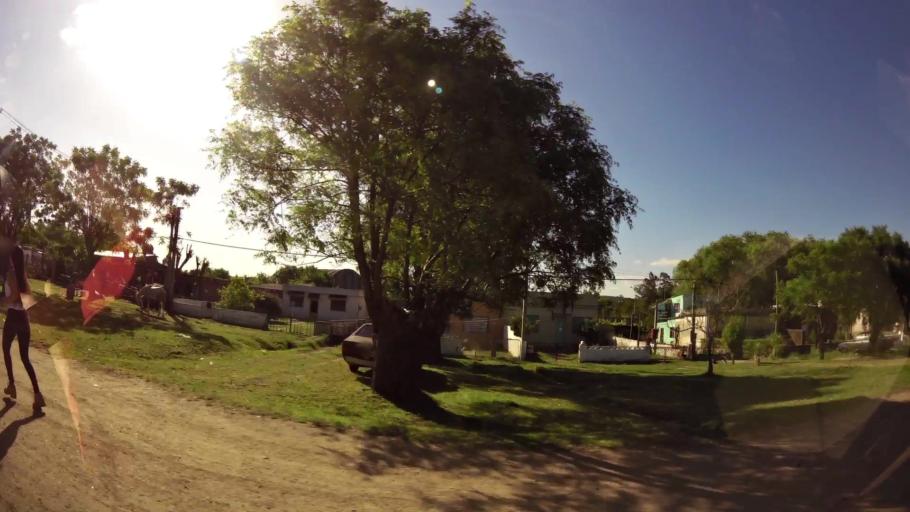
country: UY
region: Canelones
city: La Paz
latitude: -34.8174
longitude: -56.1732
